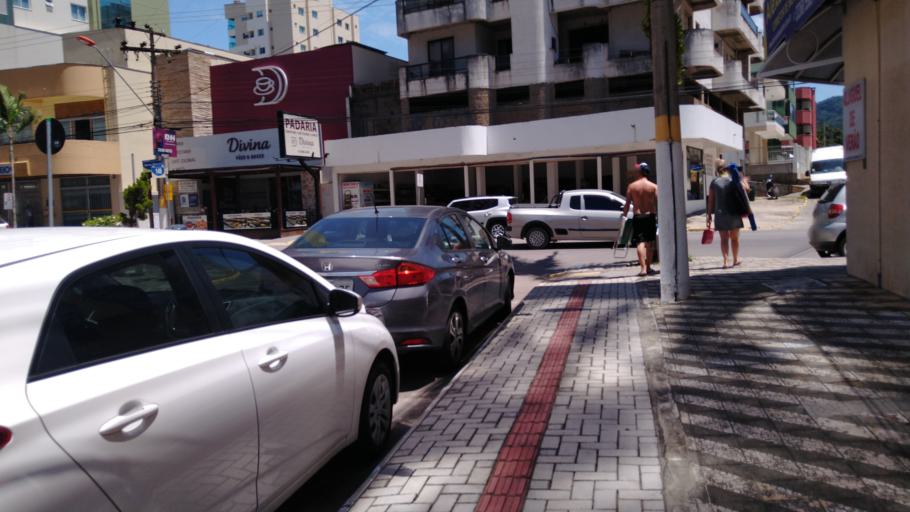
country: BR
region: Santa Catarina
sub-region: Itapema
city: Itapema
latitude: -27.1015
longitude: -48.6150
